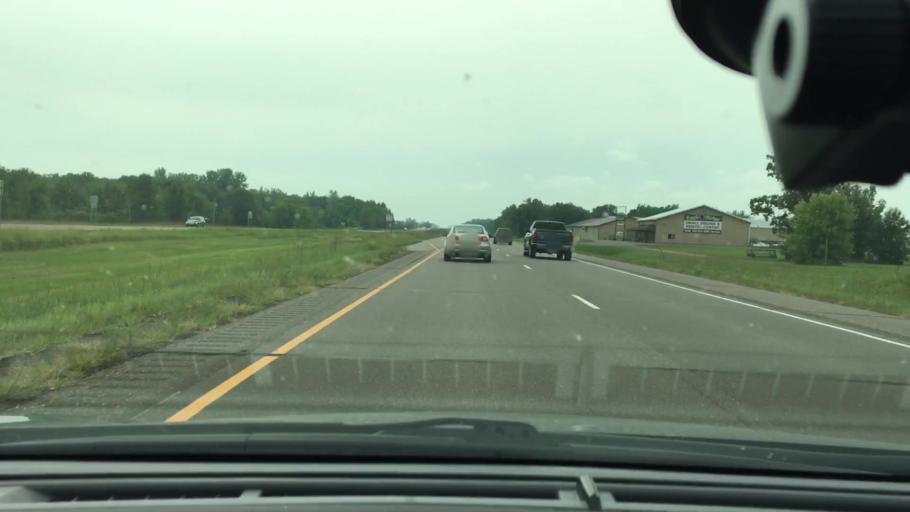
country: US
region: Minnesota
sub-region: Mille Lacs County
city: Vineland
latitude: 46.0538
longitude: -93.6628
